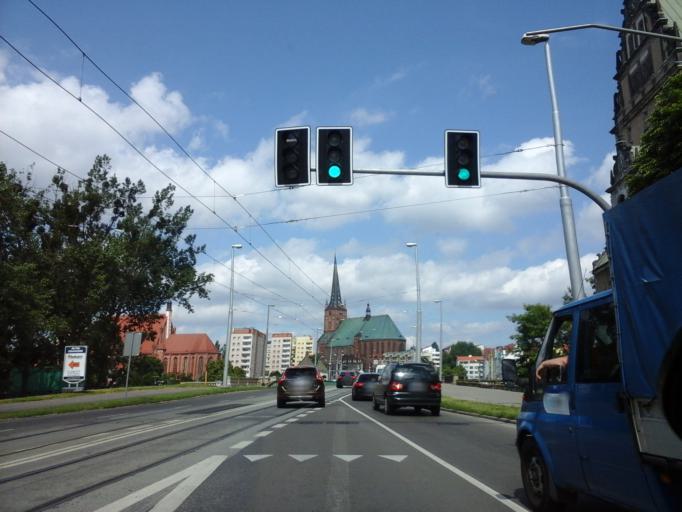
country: PL
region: West Pomeranian Voivodeship
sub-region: Szczecin
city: Szczecin
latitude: 53.4213
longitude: 14.5619
